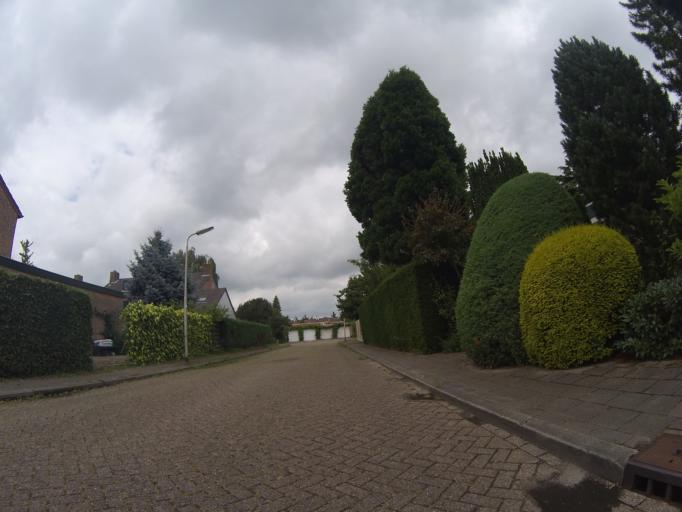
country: NL
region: Utrecht
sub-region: Gemeente Amersfoort
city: Amersfoort
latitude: 52.1713
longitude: 5.3967
